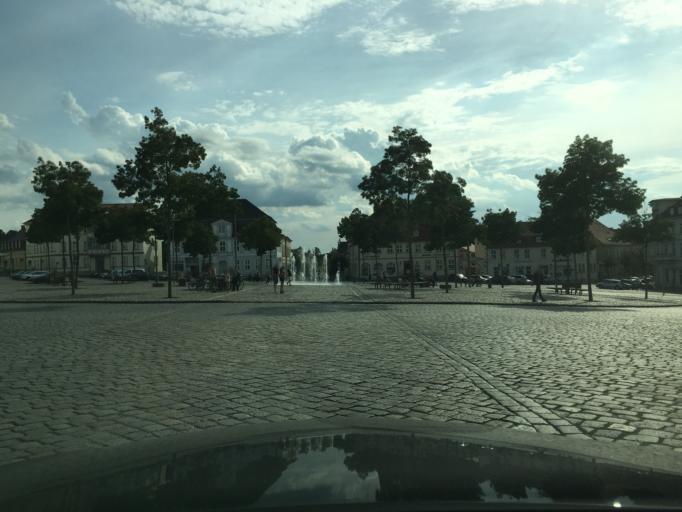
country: DE
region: Mecklenburg-Vorpommern
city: Neustrelitz
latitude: 53.3635
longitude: 13.0628
